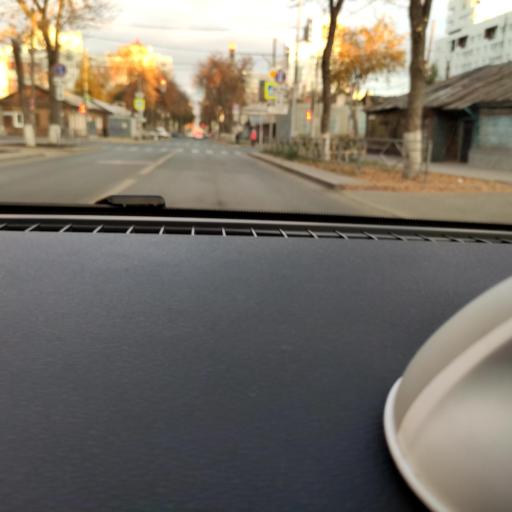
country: RU
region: Samara
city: Samara
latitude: 53.1994
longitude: 50.1197
